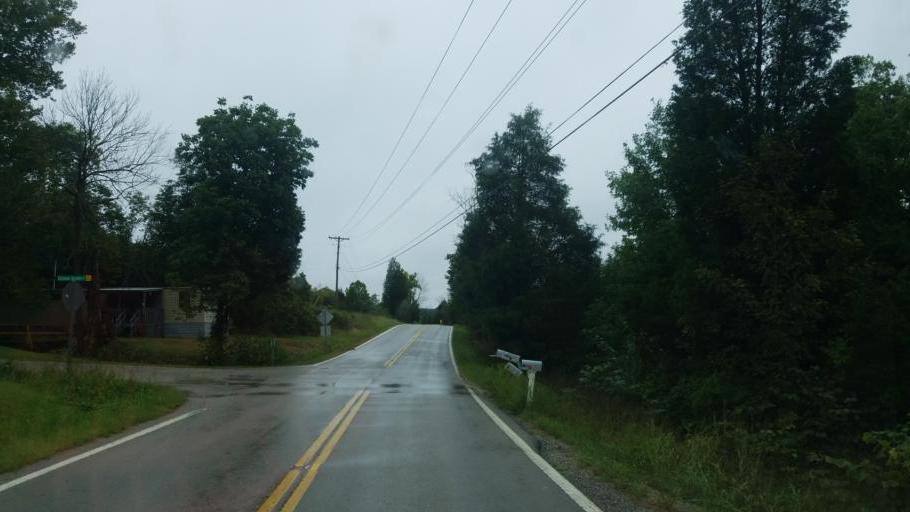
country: US
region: Ohio
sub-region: Adams County
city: West Union
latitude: 38.7762
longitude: -83.5342
